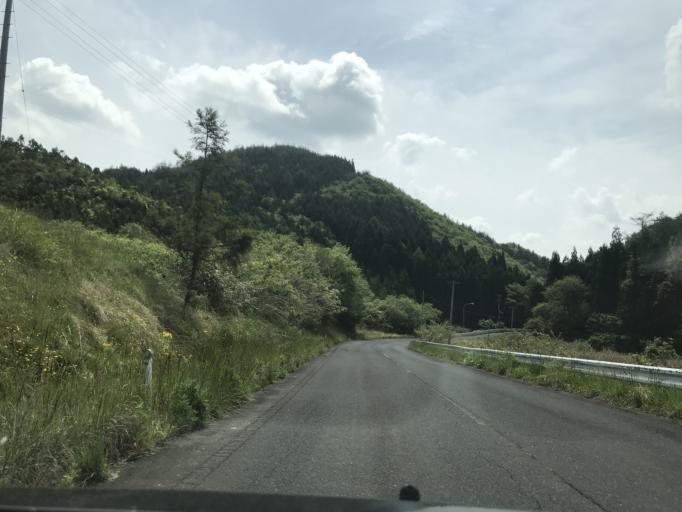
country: JP
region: Iwate
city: Ichinoseki
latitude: 38.8761
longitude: 140.9766
